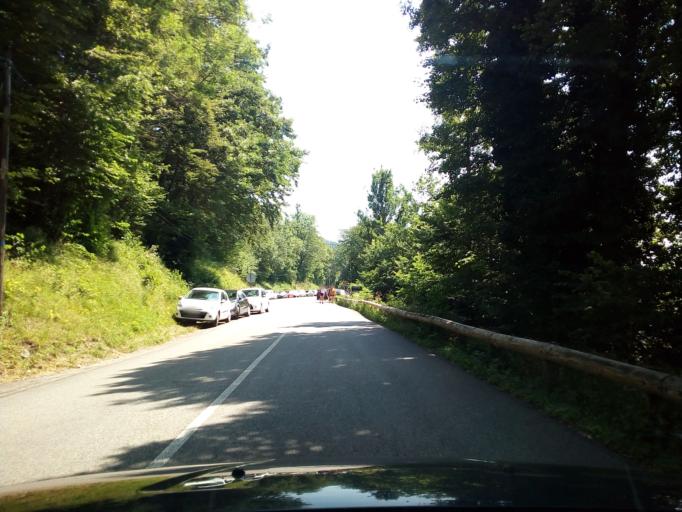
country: FR
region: Rhone-Alpes
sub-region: Departement de l'Isere
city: Notre-Dame-de-Mesage
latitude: 45.0228
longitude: 5.7832
